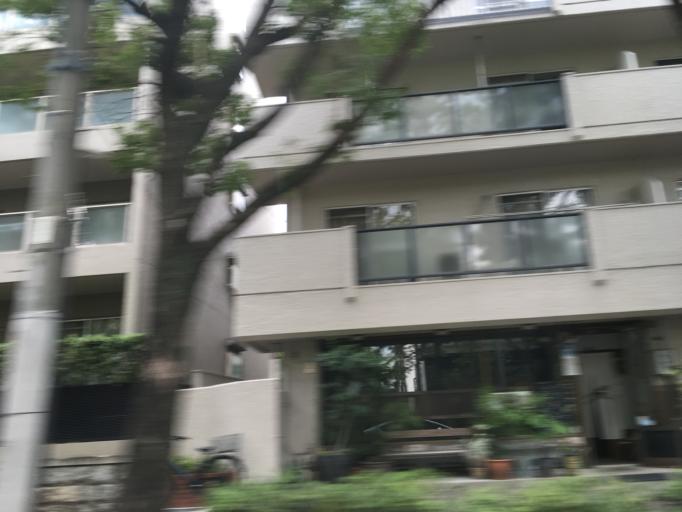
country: JP
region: Hyogo
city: Ashiya
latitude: 34.7224
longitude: 135.2574
